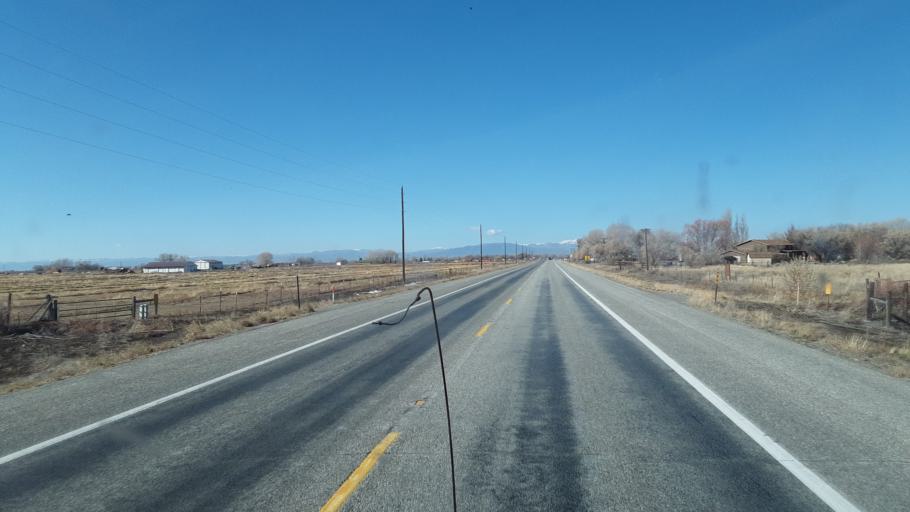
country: US
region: Colorado
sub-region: Alamosa County
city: Alamosa East
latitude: 37.4735
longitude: -105.7937
